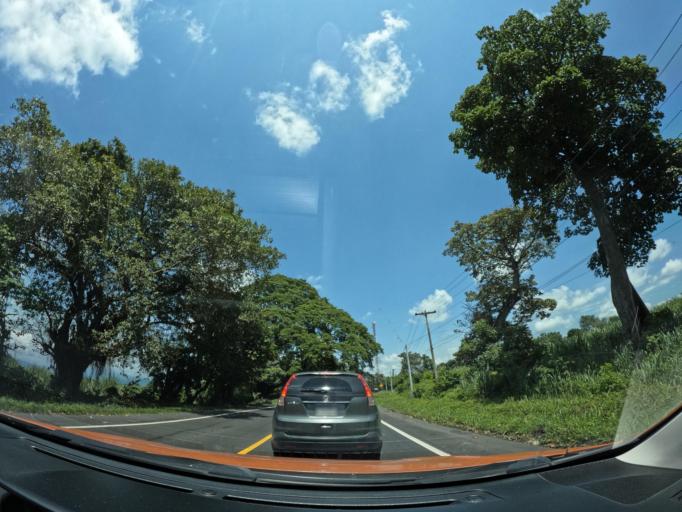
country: GT
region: Escuintla
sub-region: Municipio de Masagua
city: Masagua
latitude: 14.1972
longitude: -90.8536
